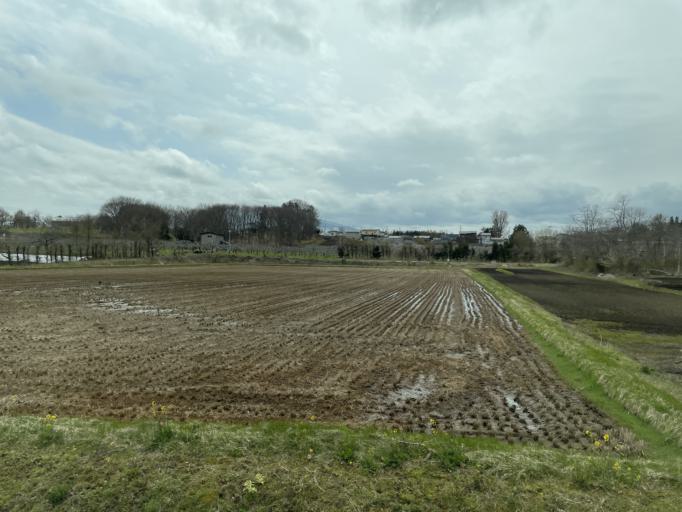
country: JP
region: Aomori
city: Shimokizukuri
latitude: 40.7872
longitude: 140.2992
